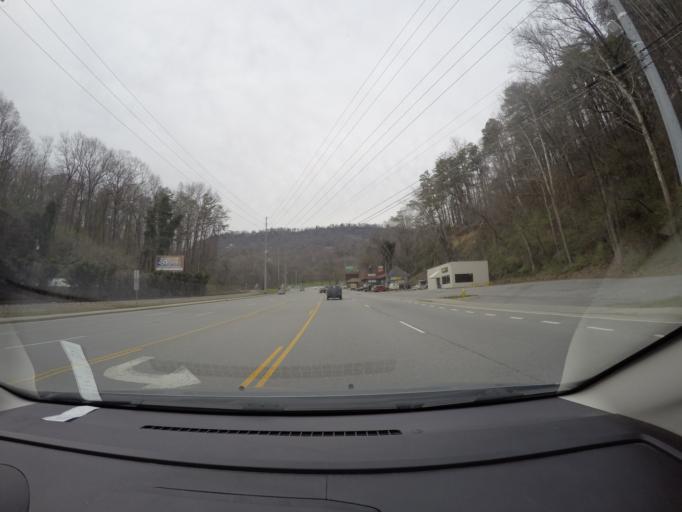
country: US
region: Tennessee
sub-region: Hamilton County
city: Signal Mountain
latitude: 35.1029
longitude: -85.3313
